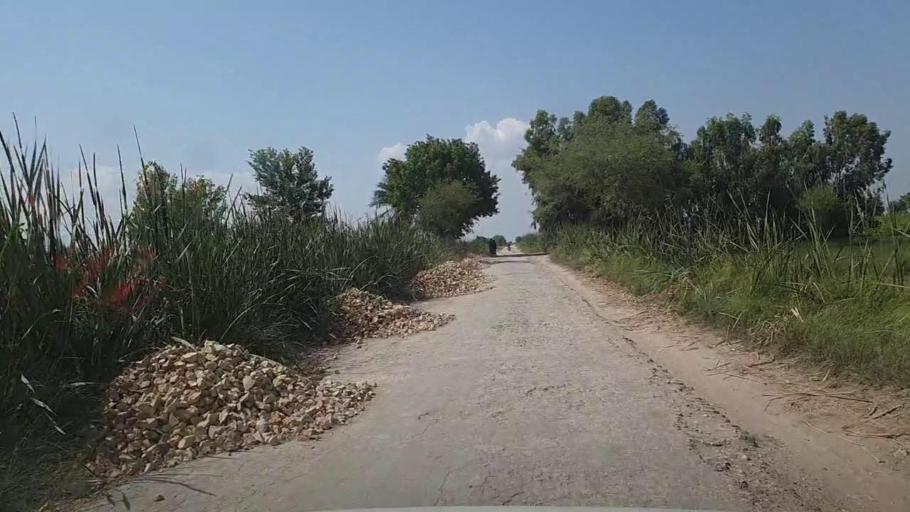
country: PK
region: Sindh
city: Khairpur
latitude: 28.0893
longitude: 69.6318
